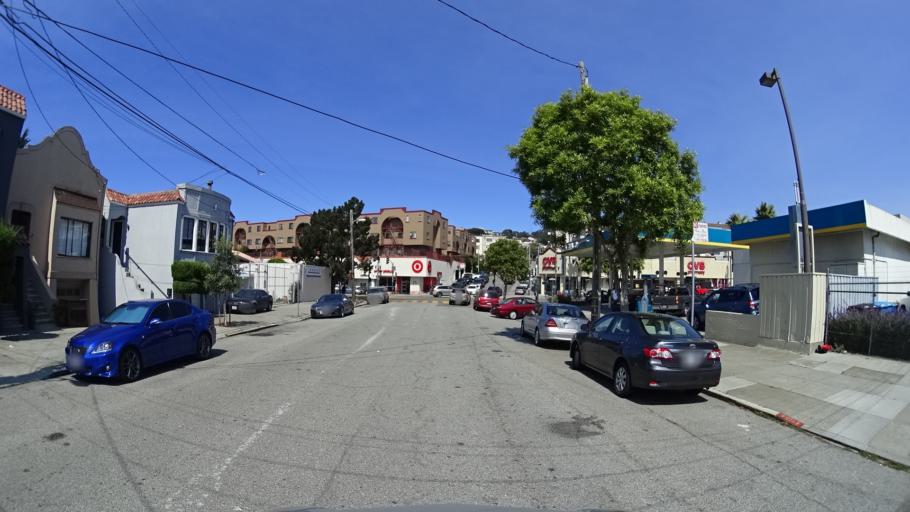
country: US
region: California
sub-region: San Mateo County
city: Daly City
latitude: 37.7244
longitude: -122.4613
